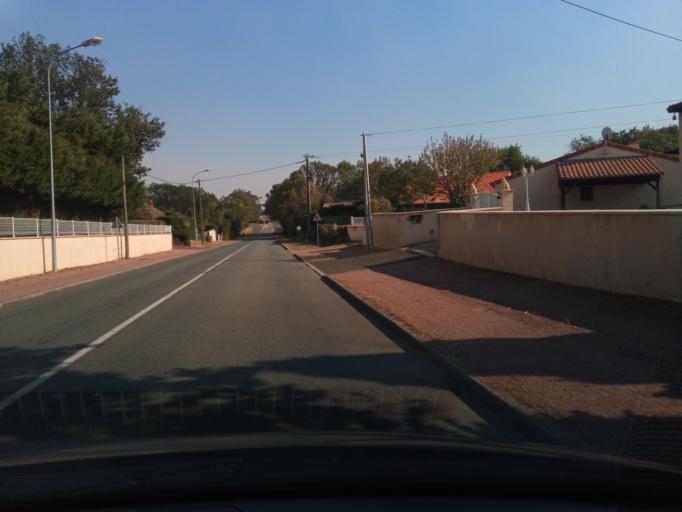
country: FR
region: Poitou-Charentes
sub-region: Departement de la Vienne
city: Montmorillon
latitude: 46.4279
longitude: 0.8561
